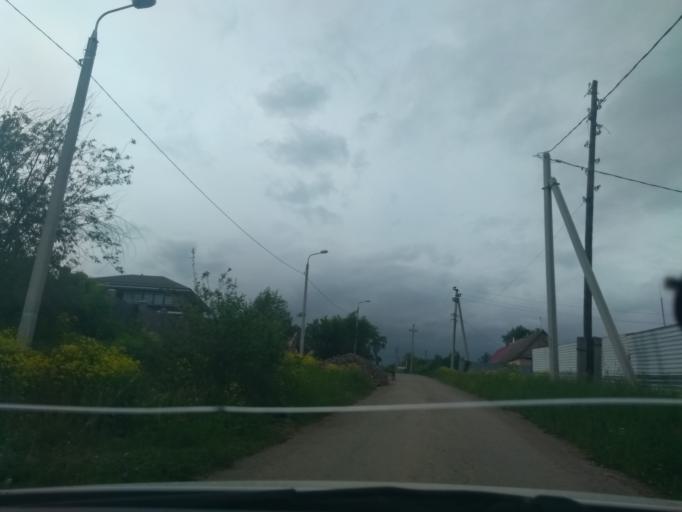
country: RU
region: Perm
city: Perm
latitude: 57.9920
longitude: 56.3384
